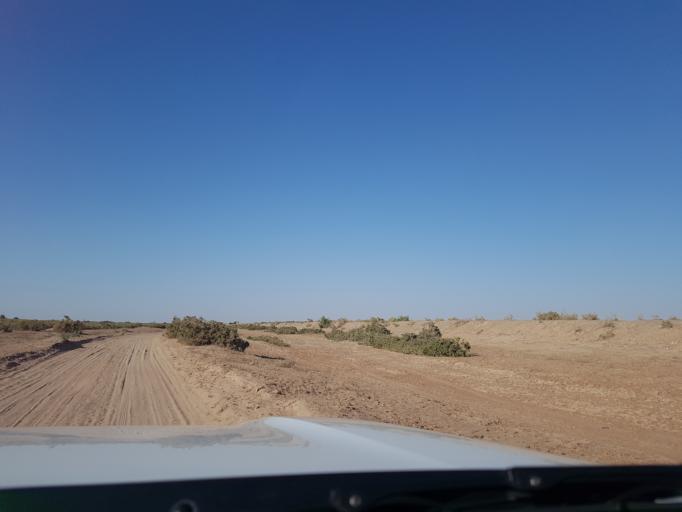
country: IR
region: Razavi Khorasan
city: Sarakhs
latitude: 36.9867
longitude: 61.3872
